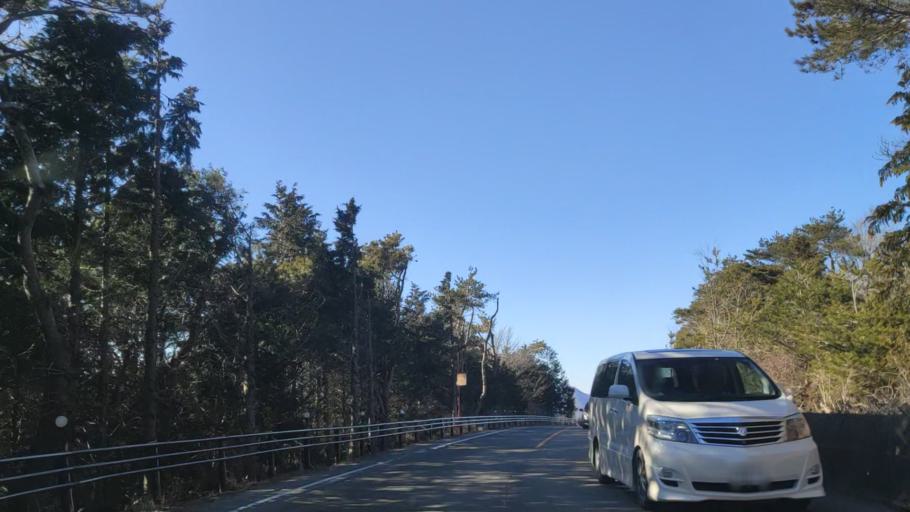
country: JP
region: Yamanashi
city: Fujikawaguchiko
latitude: 35.4395
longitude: 138.6361
